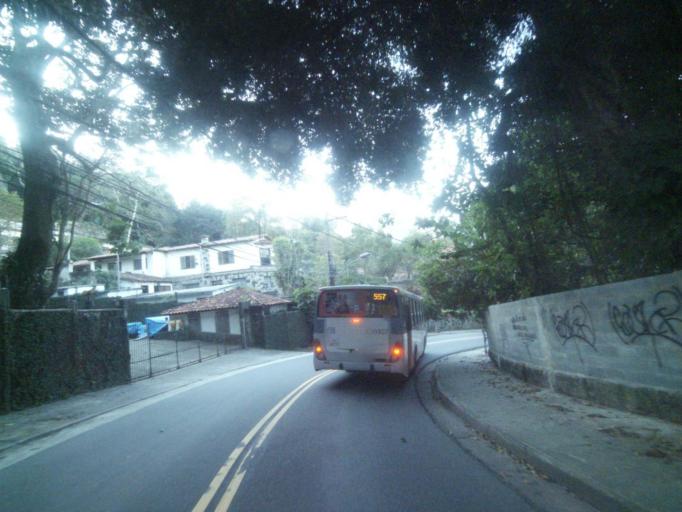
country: BR
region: Rio de Janeiro
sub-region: Rio De Janeiro
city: Rio de Janeiro
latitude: -23.0018
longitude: -43.2767
